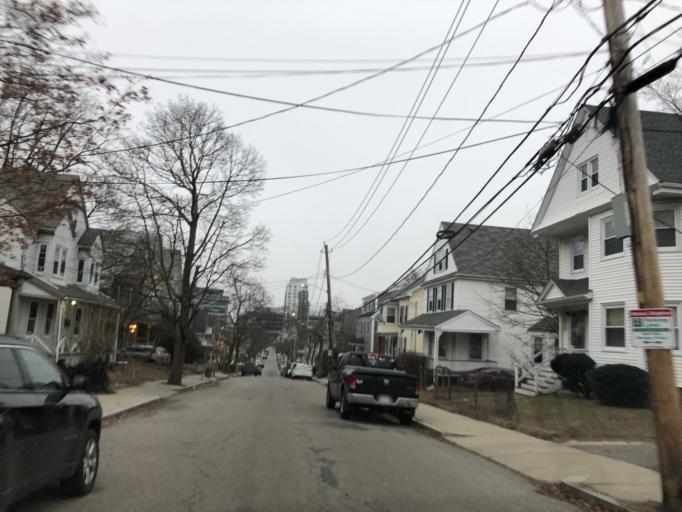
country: US
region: Massachusetts
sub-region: Norfolk County
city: Brookline
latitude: 42.3517
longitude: -71.1460
